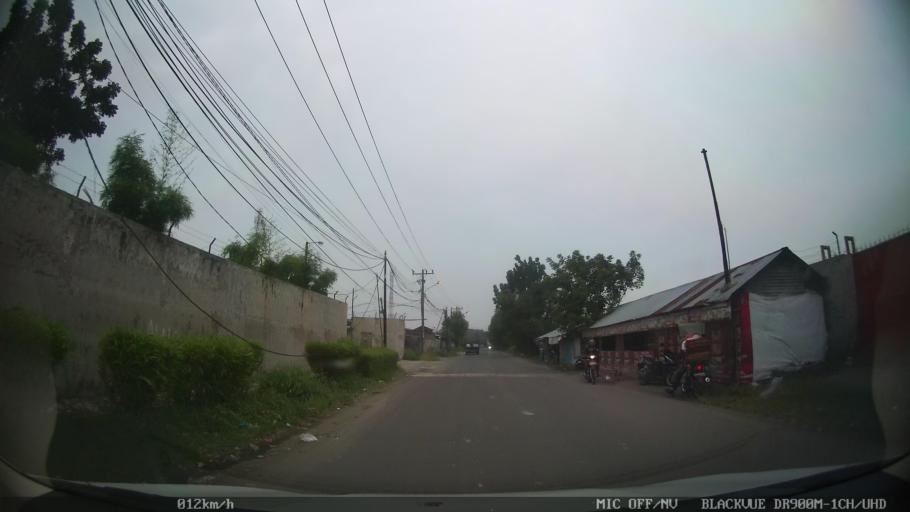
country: ID
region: North Sumatra
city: Deli Tua
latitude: 3.5372
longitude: 98.7308
